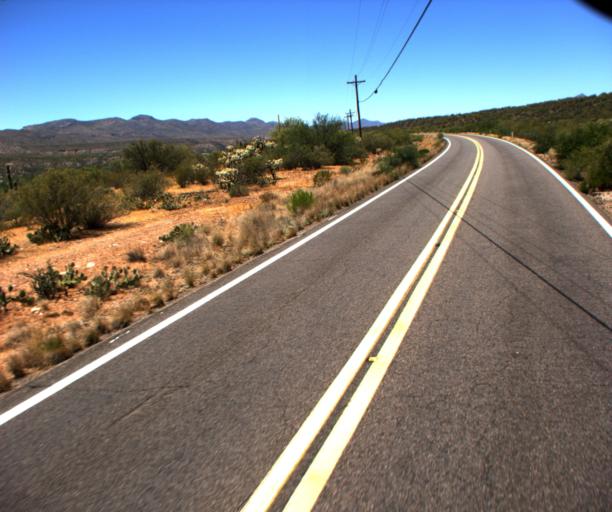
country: US
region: Arizona
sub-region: Pinal County
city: Kearny
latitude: 33.0987
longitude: -110.7332
